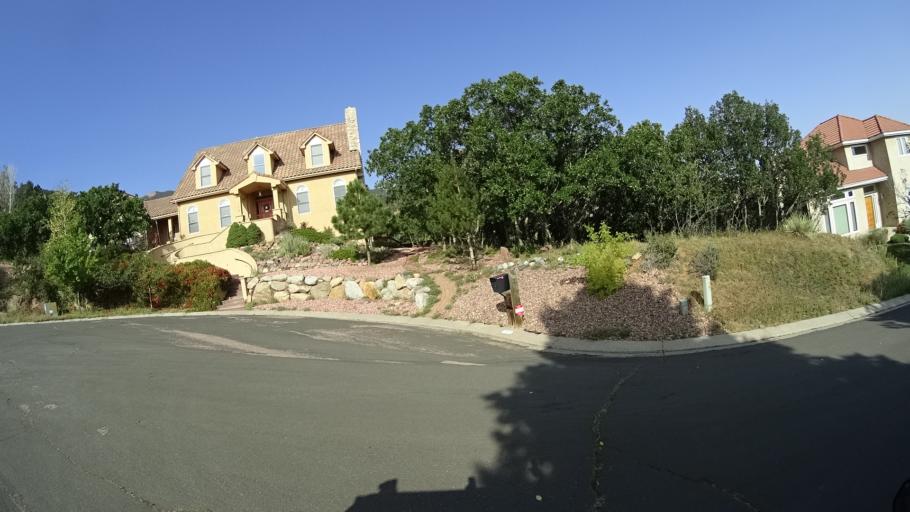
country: US
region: Colorado
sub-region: El Paso County
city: Manitou Springs
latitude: 38.8212
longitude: -104.8816
